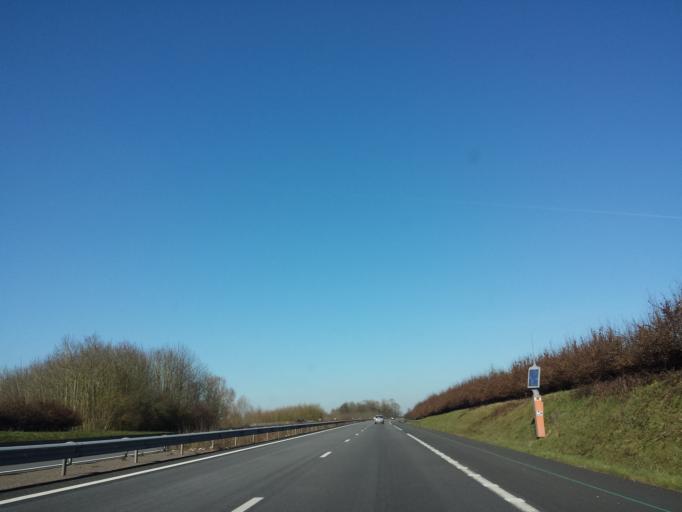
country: FR
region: Picardie
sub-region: Departement de l'Oise
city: Saint-Crepin-Ibouvillers
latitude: 49.2809
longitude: 2.0795
